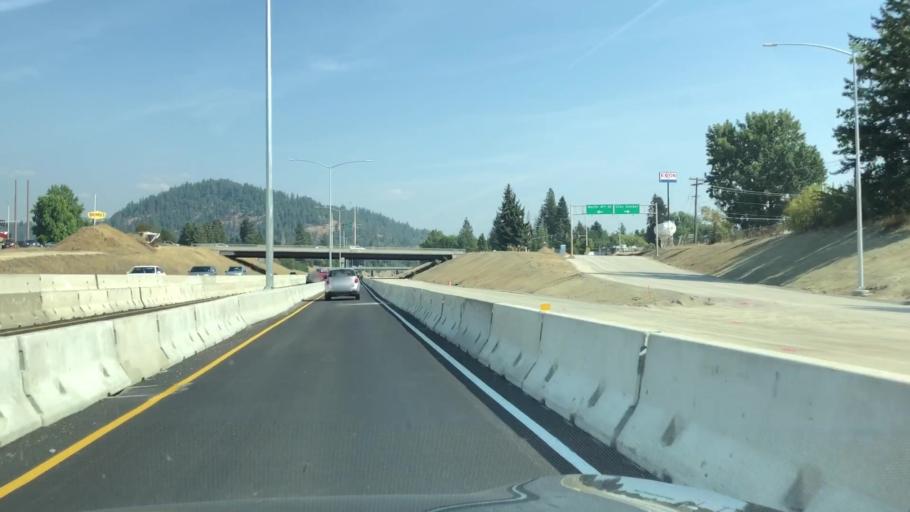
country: US
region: Idaho
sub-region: Kootenai County
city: Coeur d'Alene
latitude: 47.6980
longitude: -116.7838
